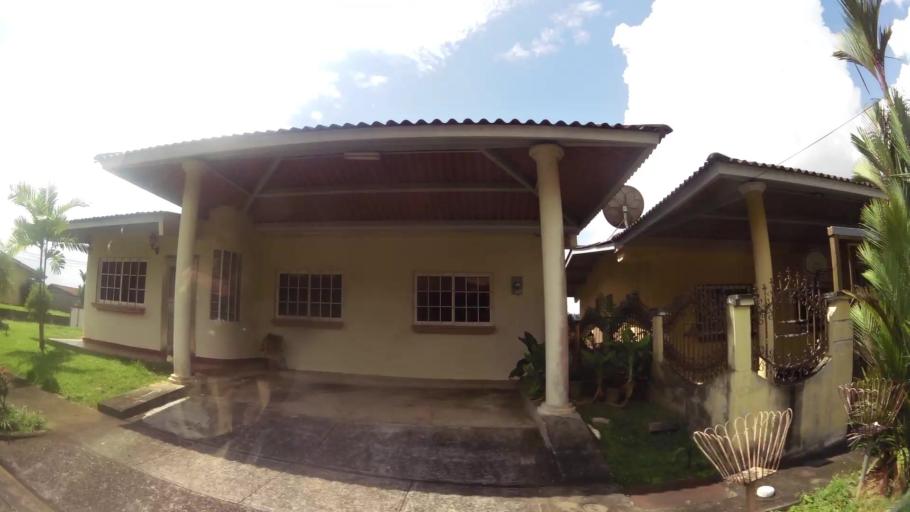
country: PA
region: Panama
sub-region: Distrito Arraijan
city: Arraijan
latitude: 8.9452
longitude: -79.6754
